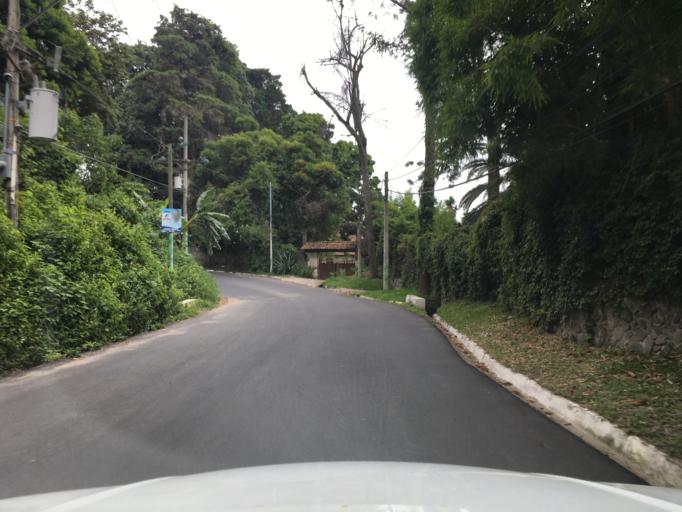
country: GT
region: Solola
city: Panajachel
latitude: 14.7343
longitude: -91.1481
